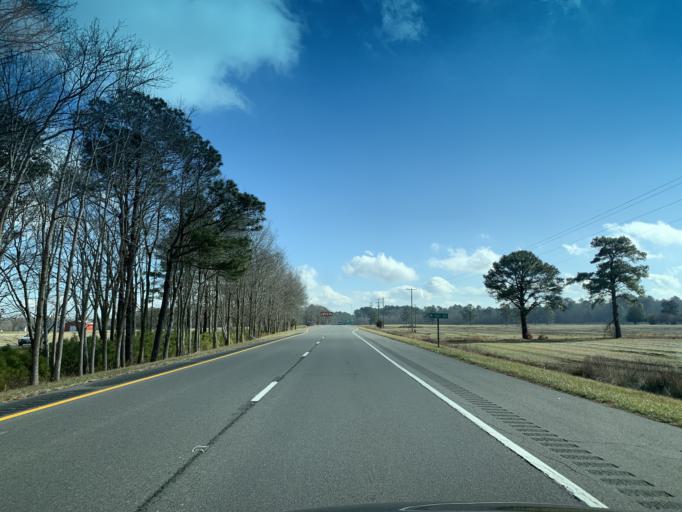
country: US
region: Maryland
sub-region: Worcester County
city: Berlin
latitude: 38.3822
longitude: -75.2990
